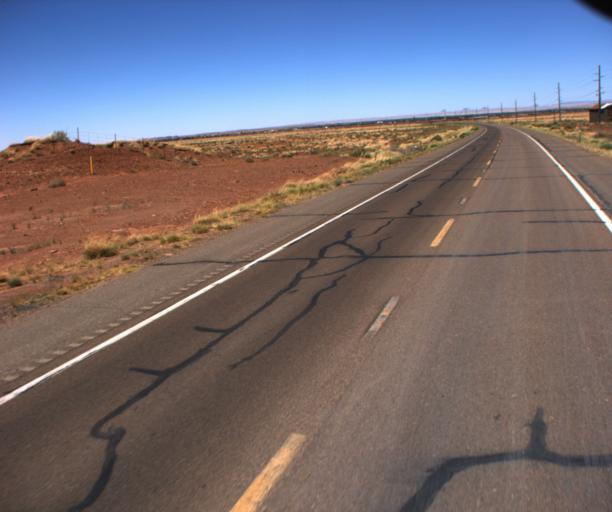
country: US
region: Arizona
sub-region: Navajo County
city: Winslow
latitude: 34.9929
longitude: -110.7084
